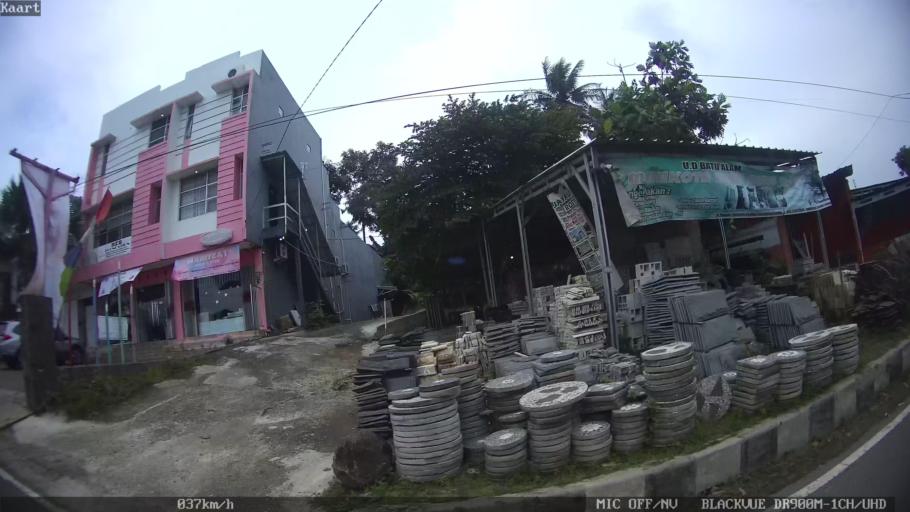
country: ID
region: Lampung
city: Kedaton
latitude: -5.3801
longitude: 105.2215
